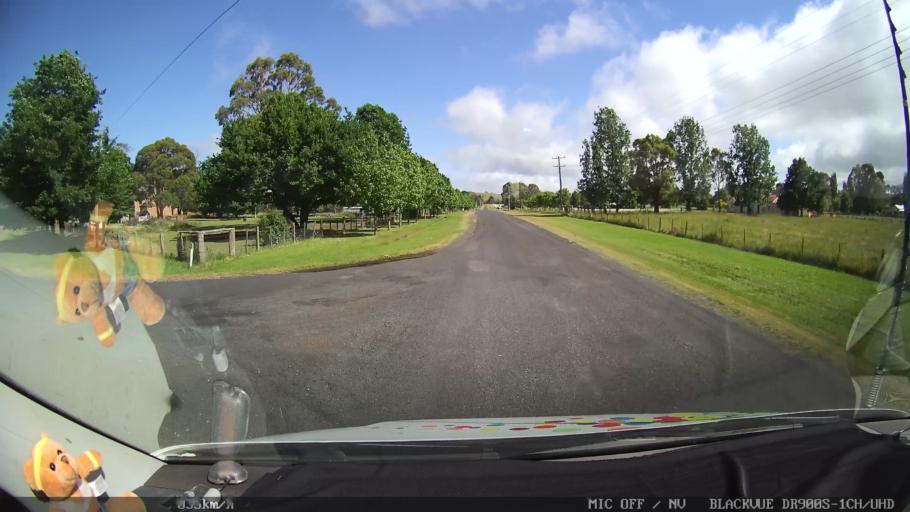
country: AU
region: New South Wales
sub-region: Guyra
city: Guyra
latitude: -30.0227
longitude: 151.6598
